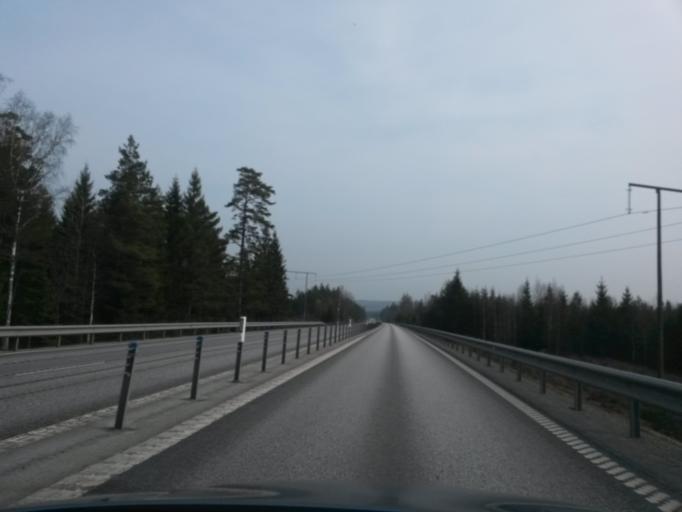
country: SE
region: Vaestra Goetaland
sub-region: Gullspangs Kommun
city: Anderstorp
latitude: 58.9129
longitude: 14.3783
